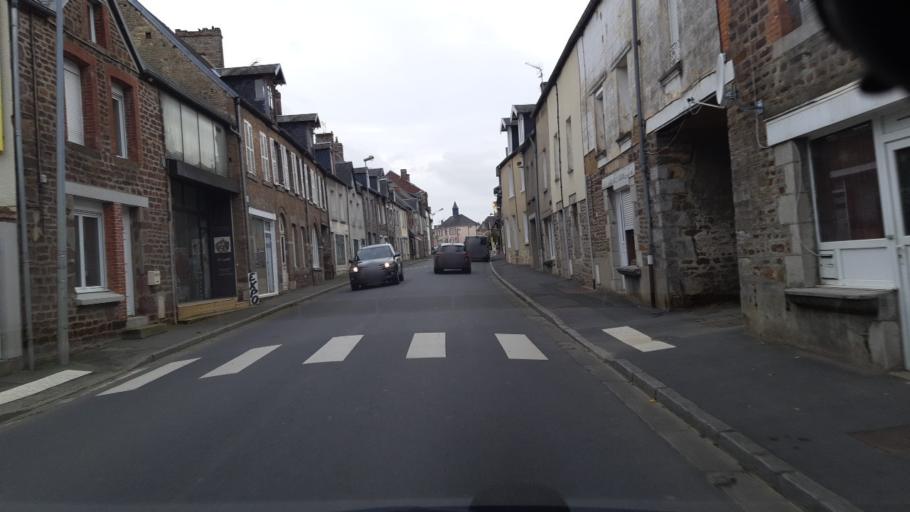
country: FR
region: Lower Normandy
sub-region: Departement de la Manche
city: Quettreville-sur-Sienne
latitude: 48.9177
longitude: -1.4333
